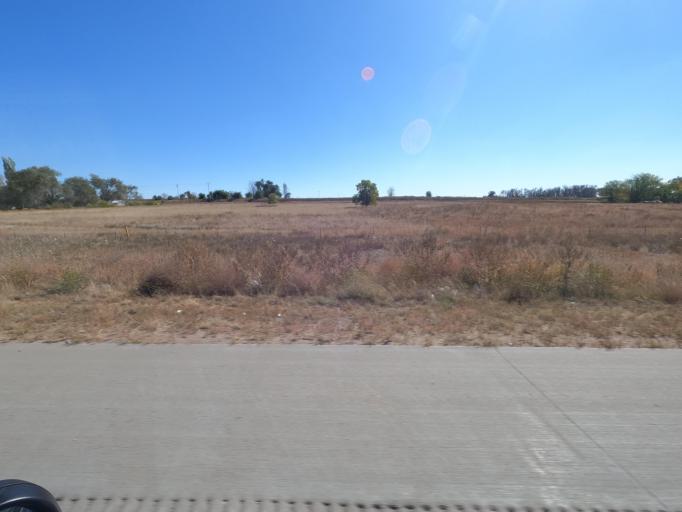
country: US
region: Colorado
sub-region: Morgan County
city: Fort Morgan
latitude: 40.2632
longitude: -103.7505
